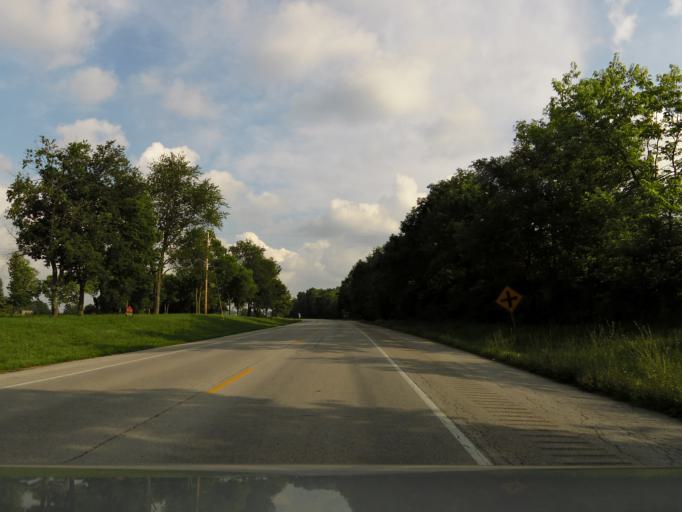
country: US
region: Kentucky
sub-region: Bourbon County
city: Paris
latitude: 38.2759
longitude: -84.2998
